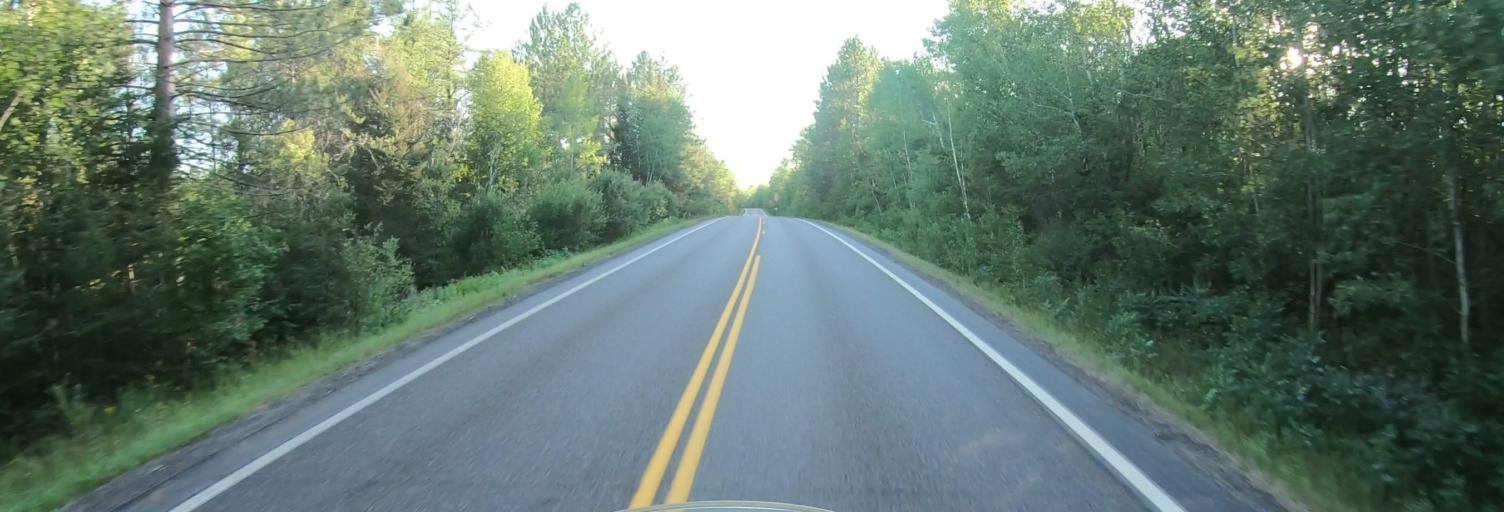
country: US
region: Minnesota
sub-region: Saint Louis County
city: Ely
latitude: 47.9566
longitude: -91.6349
